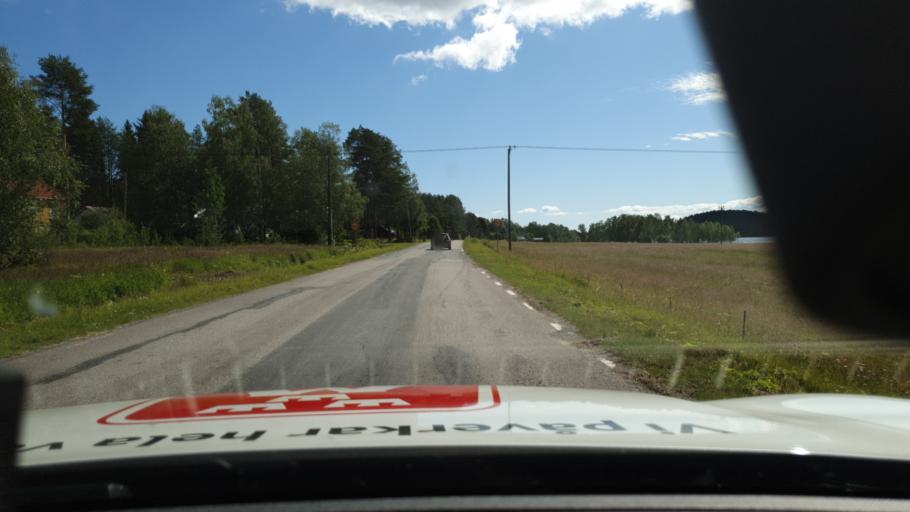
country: SE
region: Norrbotten
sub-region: Lulea Kommun
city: Ranea
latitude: 65.7749
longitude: 22.2390
